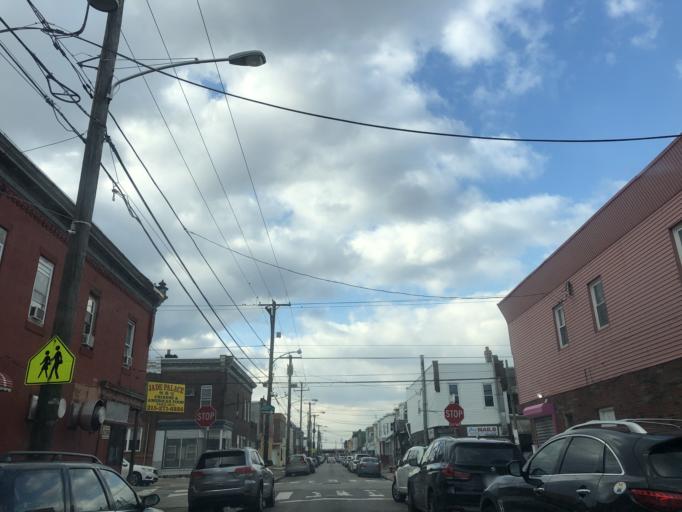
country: US
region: Pennsylvania
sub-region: Philadelphia County
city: Philadelphia
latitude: 39.9272
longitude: -75.1821
